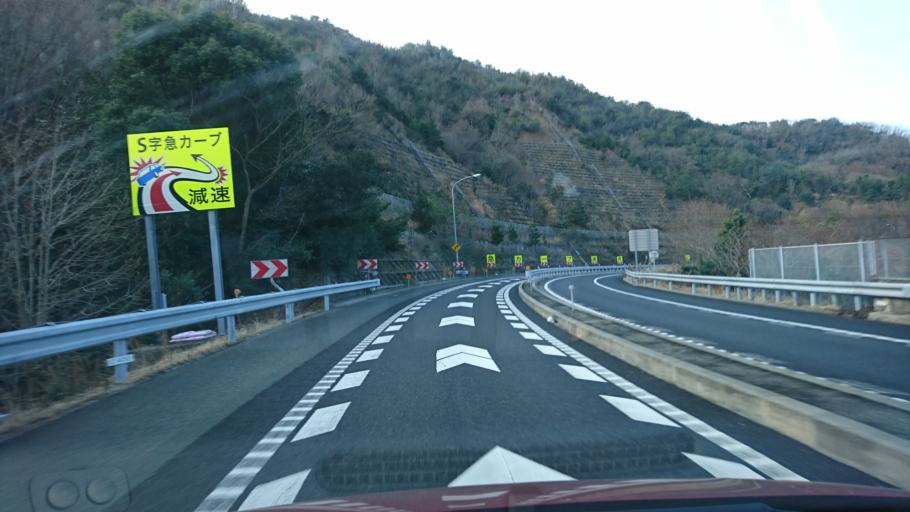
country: JP
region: Hyogo
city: Himeji
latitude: 34.8509
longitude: 134.7409
